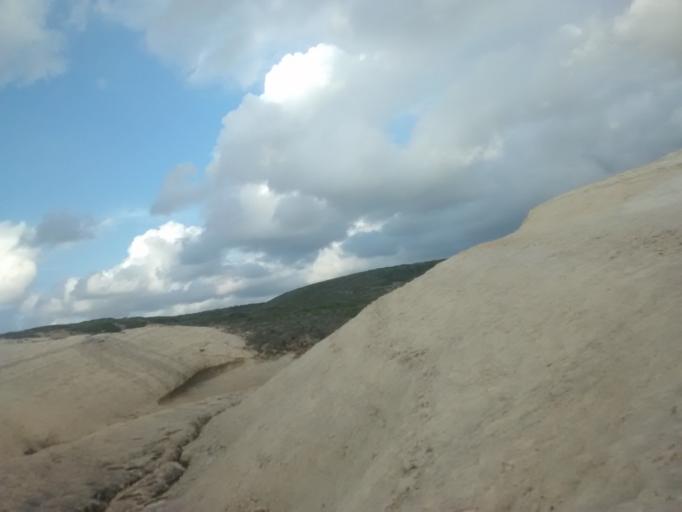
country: IT
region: Sardinia
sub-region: Provincia di Oristano
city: Narbolia
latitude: 40.0964
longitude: 8.4867
